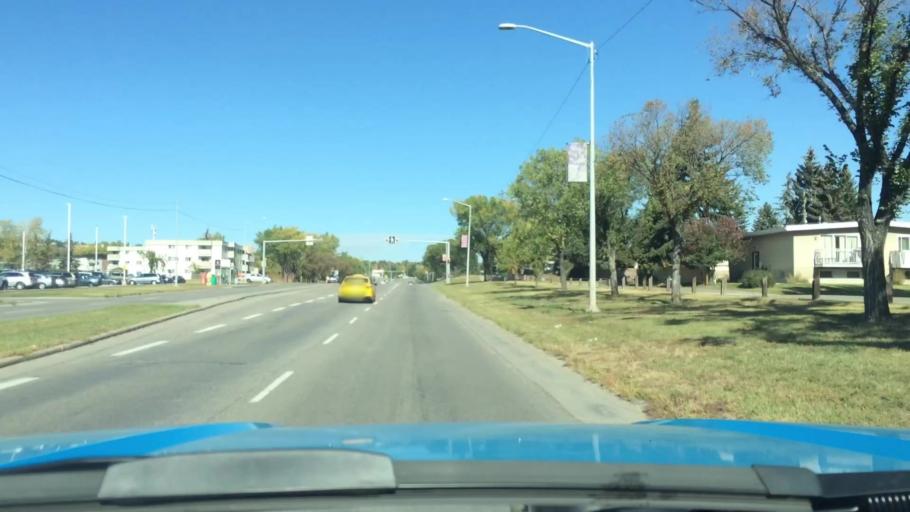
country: CA
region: Alberta
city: Calgary
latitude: 51.1125
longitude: -114.0634
